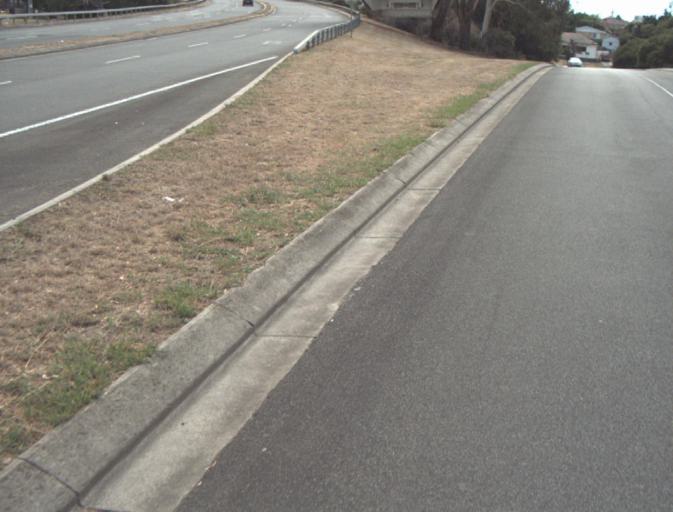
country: AU
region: Tasmania
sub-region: Launceston
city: Newnham
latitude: -41.3960
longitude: 147.1237
